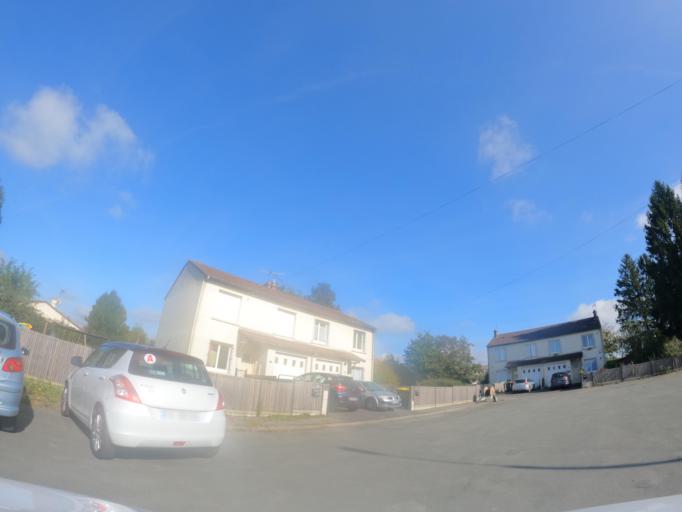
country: FR
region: Poitou-Charentes
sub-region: Departement des Deux-Sevres
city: Courlay
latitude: 46.7820
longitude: -0.5681
